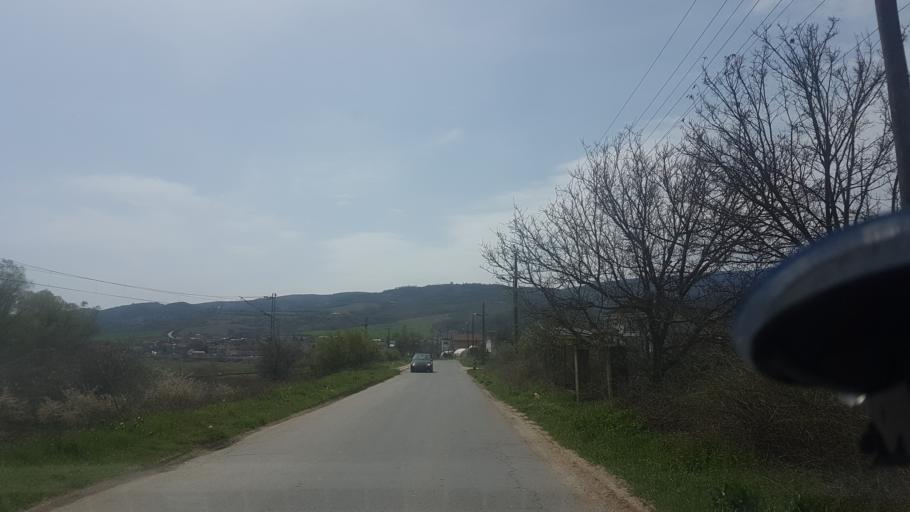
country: MK
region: Zelenikovo
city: Zelenikovo
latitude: 41.8884
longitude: 21.5879
